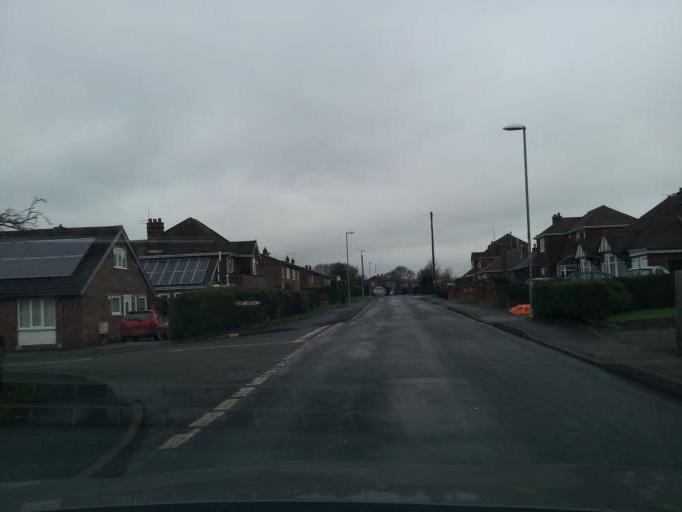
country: GB
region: England
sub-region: Leicestershire
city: Donisthorpe
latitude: 52.7452
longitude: -1.5154
